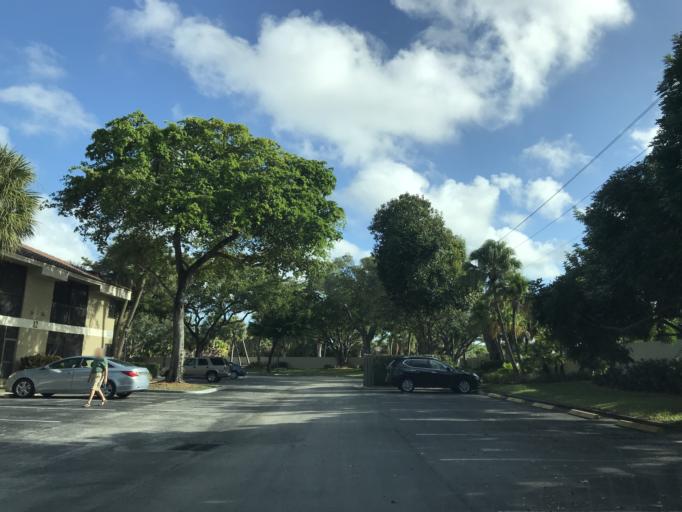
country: US
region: Florida
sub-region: Broward County
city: Coconut Creek
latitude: 26.2593
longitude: -80.1913
